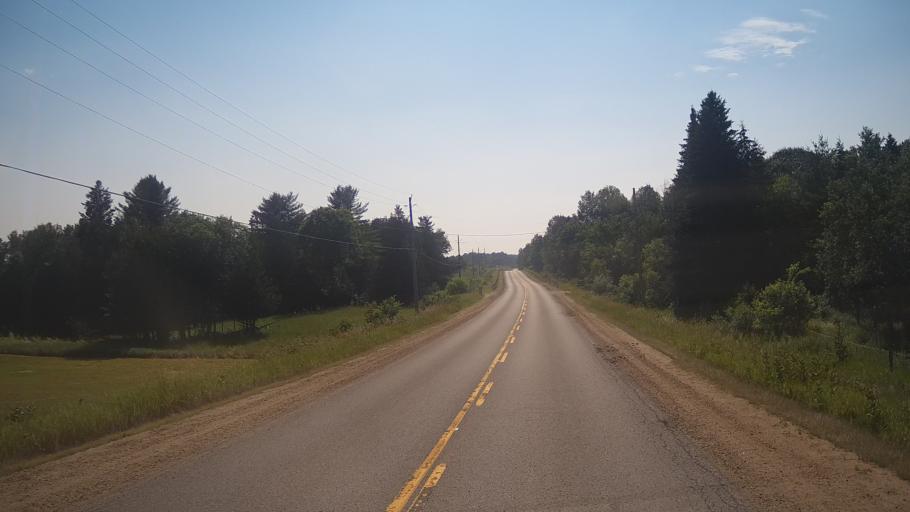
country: CA
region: Ontario
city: Pembroke
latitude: 45.6119
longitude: -77.1979
